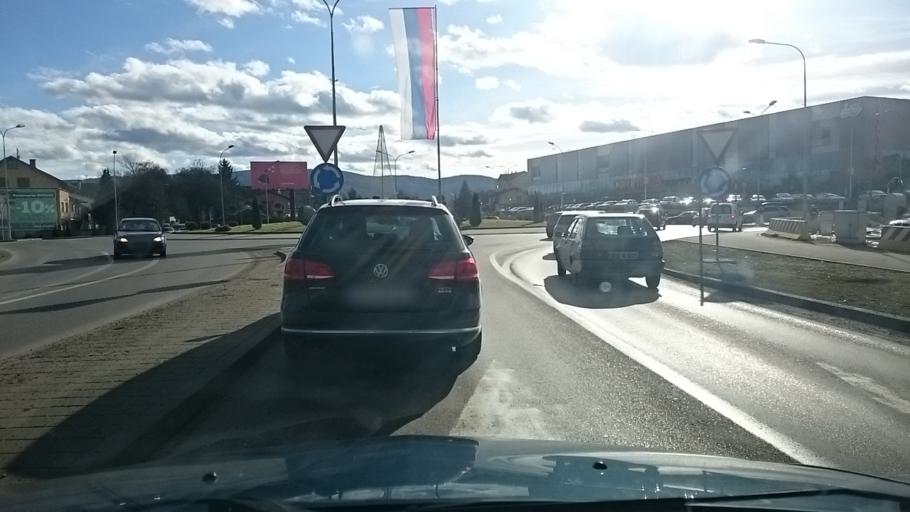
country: BA
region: Republika Srpska
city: Banja Luka
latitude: 44.7912
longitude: 17.1992
